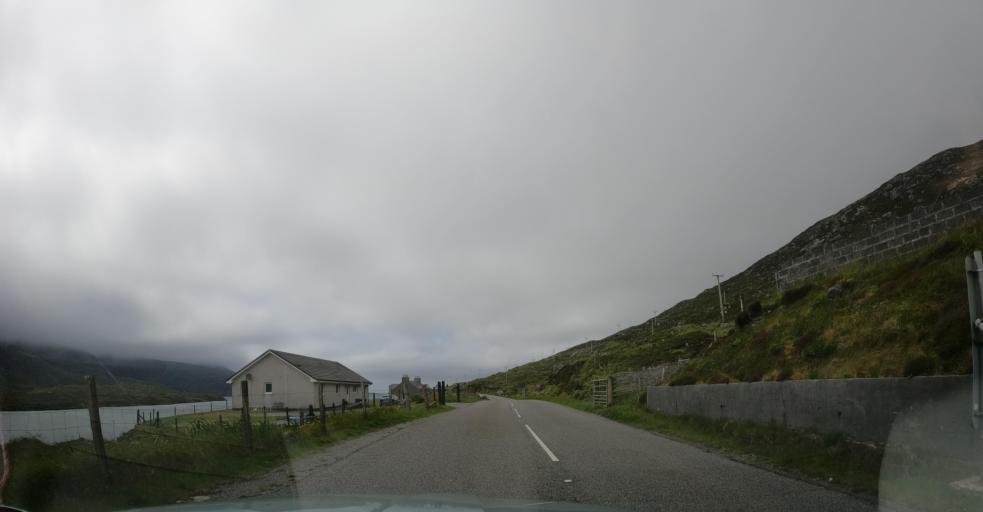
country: GB
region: Scotland
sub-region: Eilean Siar
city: Harris
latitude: 57.9053
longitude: -6.8245
